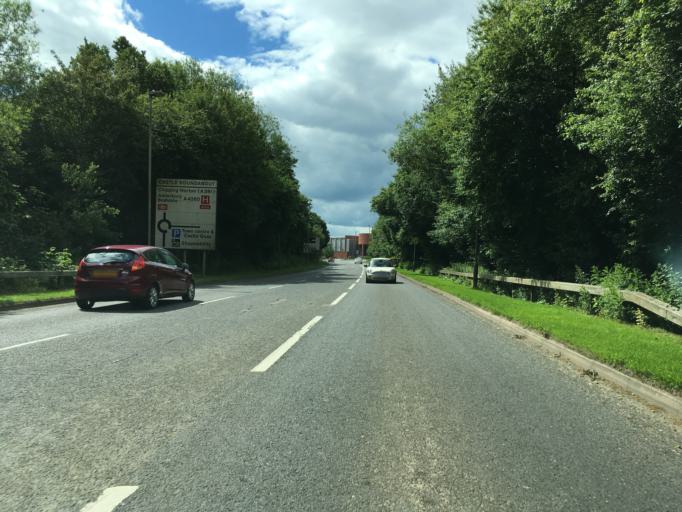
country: GB
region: England
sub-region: Oxfordshire
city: Banbury
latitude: 52.0675
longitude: -1.3311
